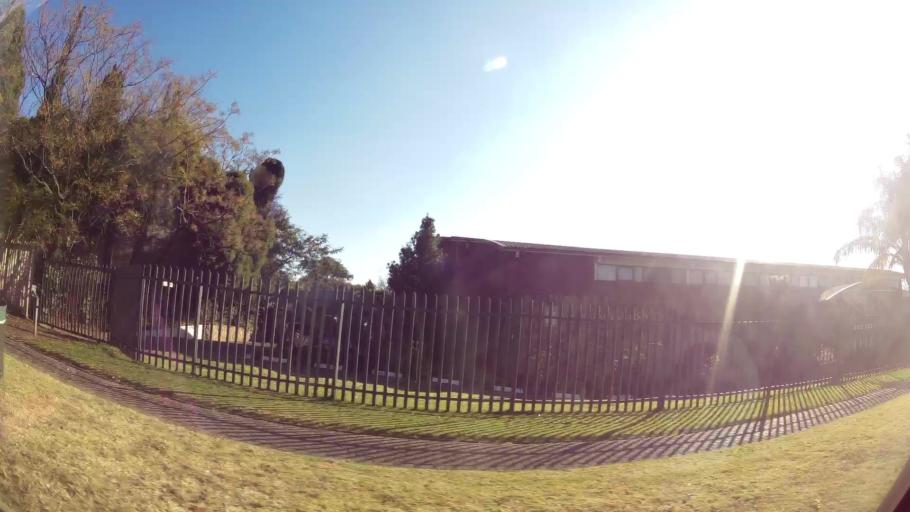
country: ZA
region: Gauteng
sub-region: Ekurhuleni Metropolitan Municipality
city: Germiston
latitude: -26.1968
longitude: 28.1239
